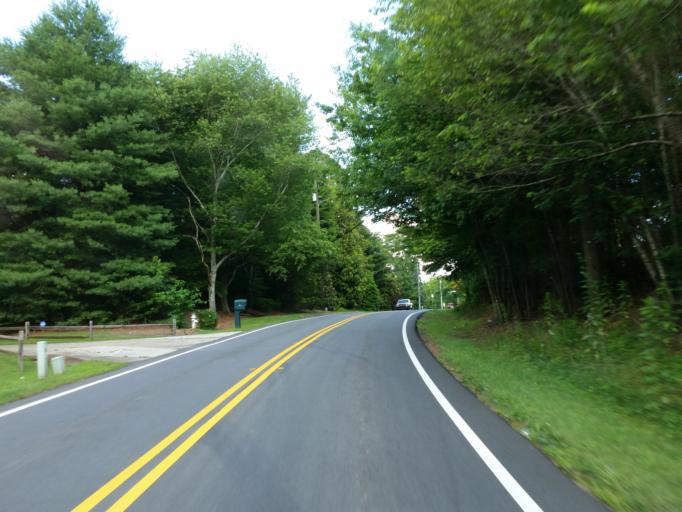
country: US
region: Georgia
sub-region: Fulton County
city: Roswell
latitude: 34.0612
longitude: -84.3443
